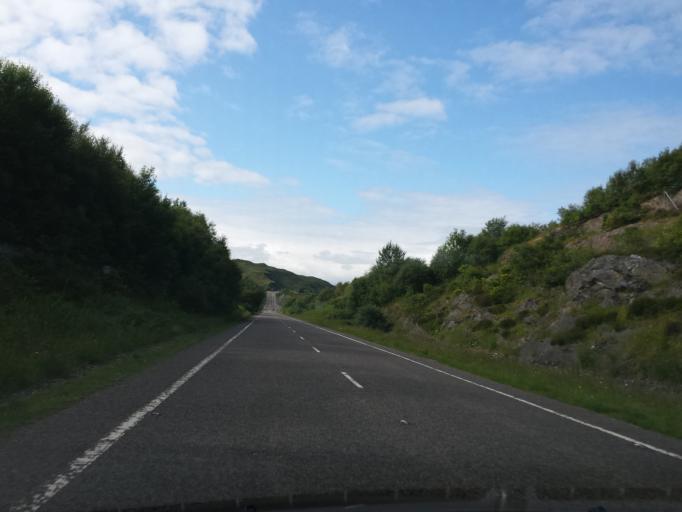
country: GB
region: Scotland
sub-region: Argyll and Bute
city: Isle Of Mull
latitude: 56.9692
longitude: -5.8250
